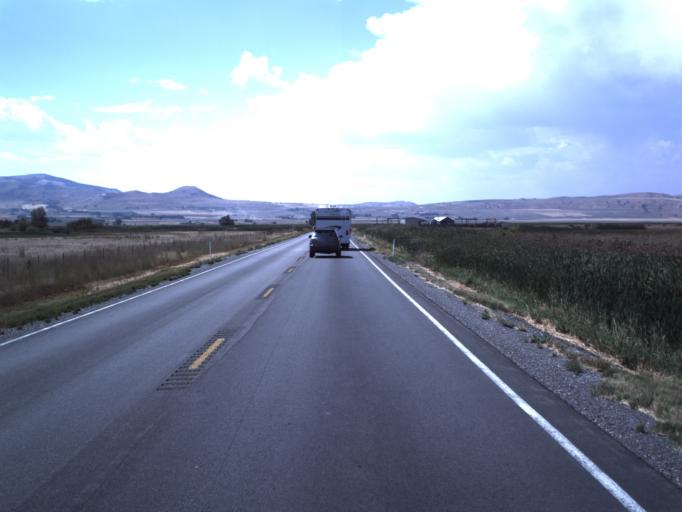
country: US
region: Utah
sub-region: Cache County
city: Benson
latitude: 41.7437
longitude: -111.9200
